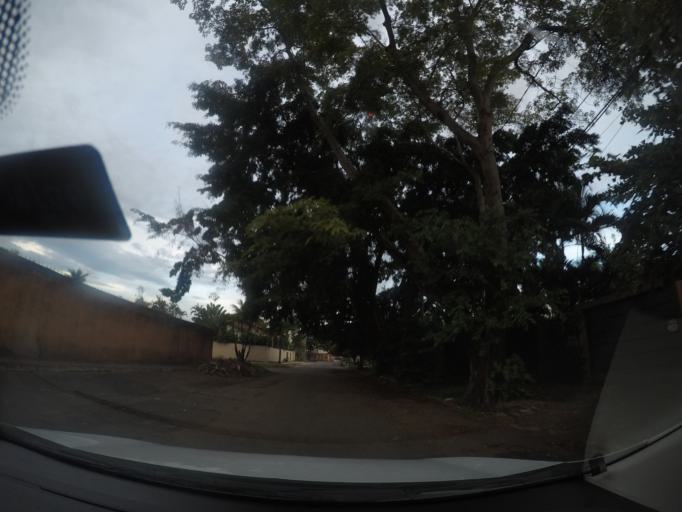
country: BR
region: Goias
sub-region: Goiania
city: Goiania
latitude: -16.6510
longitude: -49.2262
